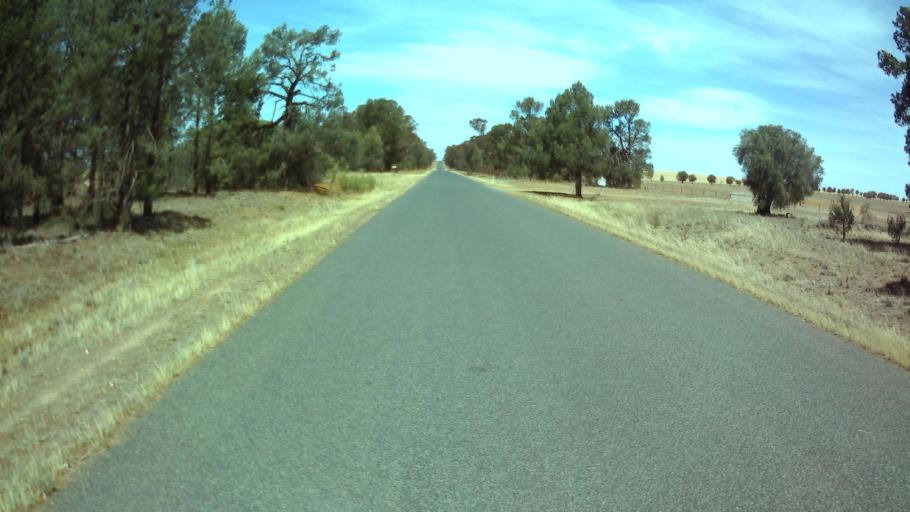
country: AU
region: New South Wales
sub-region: Weddin
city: Grenfell
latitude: -33.8940
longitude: 147.7475
